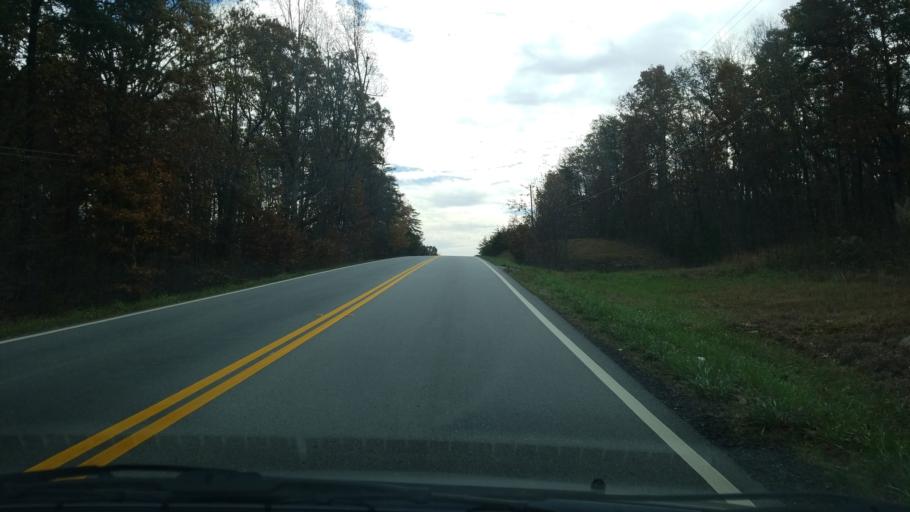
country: US
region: Georgia
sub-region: Dade County
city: Trenton
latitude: 34.8232
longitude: -85.5001
